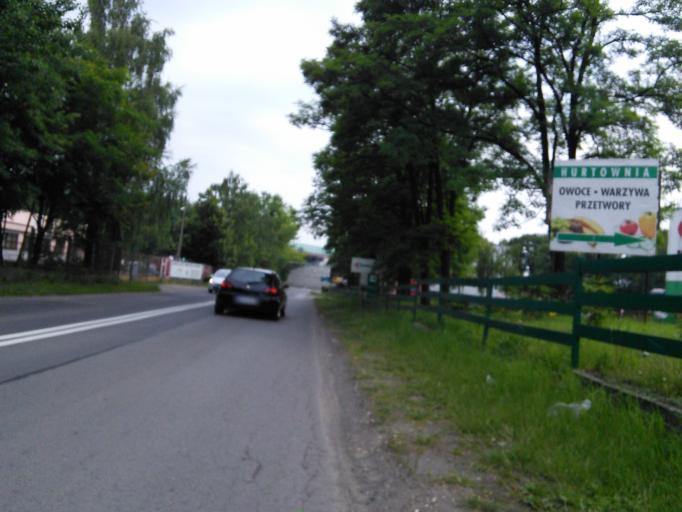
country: PL
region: Silesian Voivodeship
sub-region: Powiat bedzinski
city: Bobrowniki
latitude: 50.3734
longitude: 18.9602
